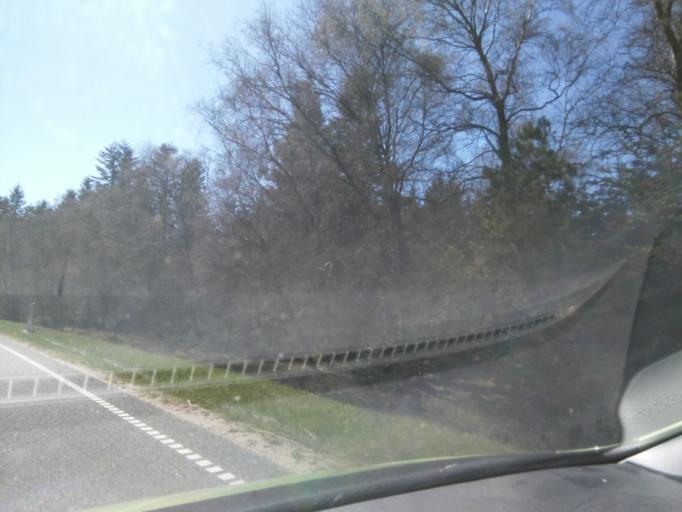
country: DK
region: South Denmark
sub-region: Varde Kommune
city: Oksbol
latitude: 55.5904
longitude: 8.2265
